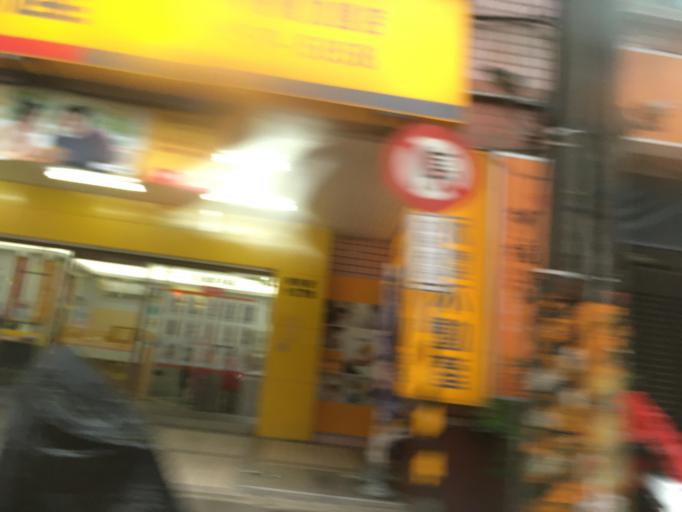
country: TW
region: Taiwan
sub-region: Keelung
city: Keelung
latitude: 25.1005
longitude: 121.7360
